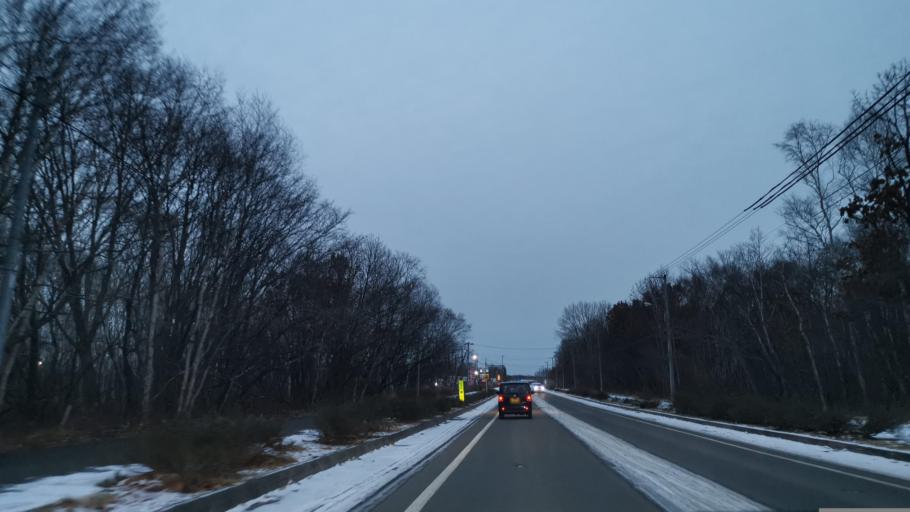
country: JP
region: Hokkaido
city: Chitose
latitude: 42.8165
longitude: 141.6711
